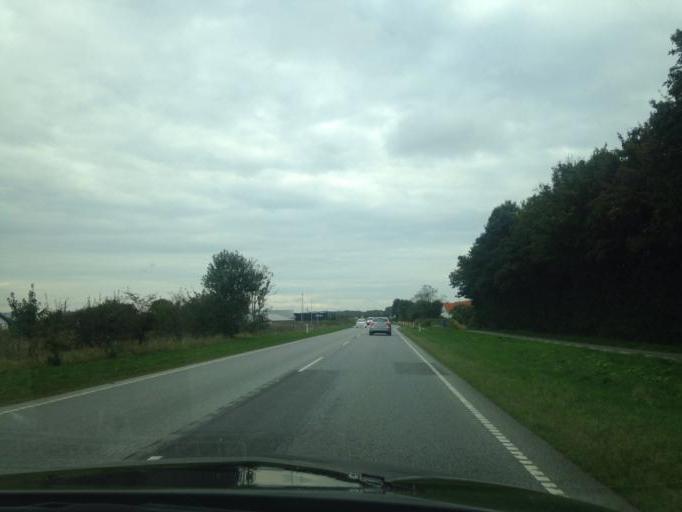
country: DK
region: South Denmark
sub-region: Haderslev Kommune
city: Vojens
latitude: 55.2476
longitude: 9.3864
